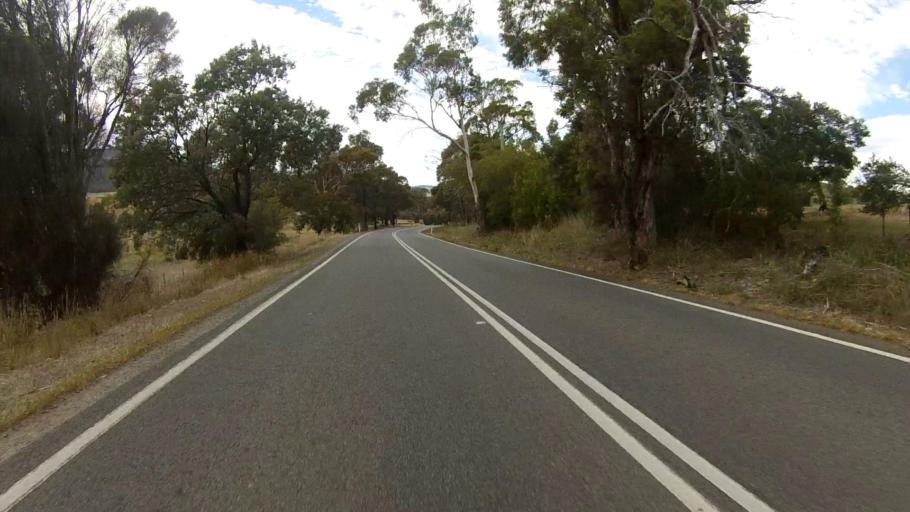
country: AU
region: Tasmania
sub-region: Sorell
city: Sorell
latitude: -42.7068
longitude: 147.5015
